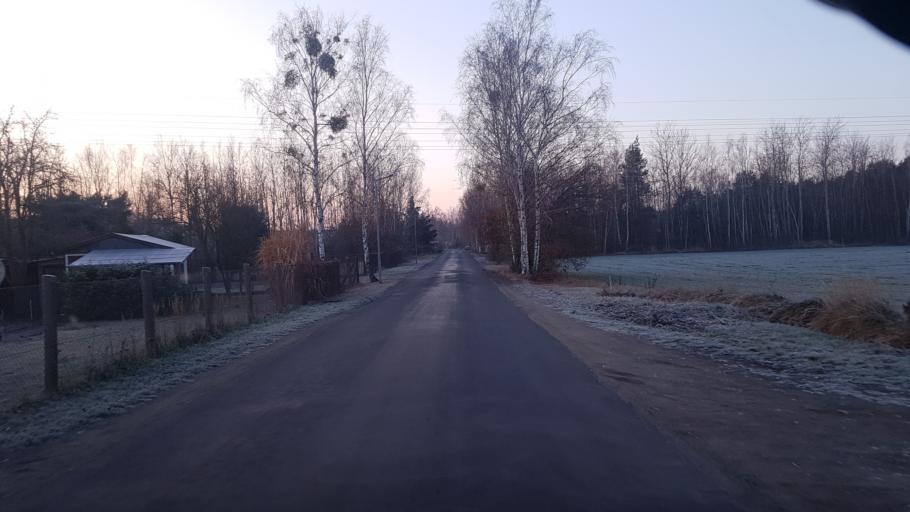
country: DE
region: Brandenburg
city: Lauchhammer
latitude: 51.5078
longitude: 13.7556
